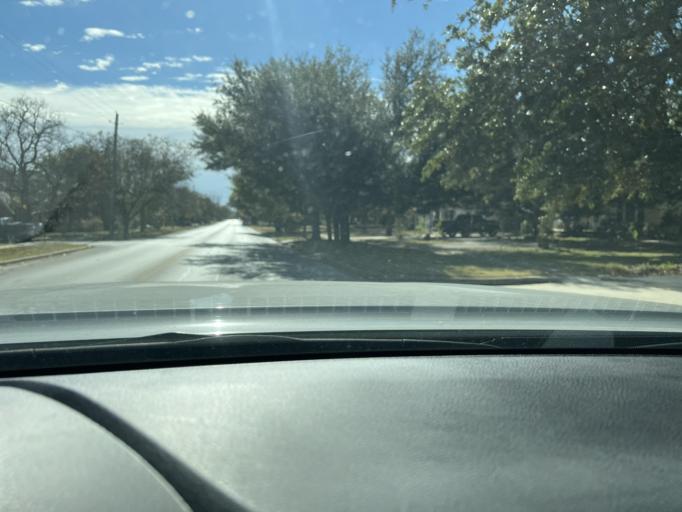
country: US
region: Texas
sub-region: Eastland County
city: Eastland
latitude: 32.3949
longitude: -98.8181
